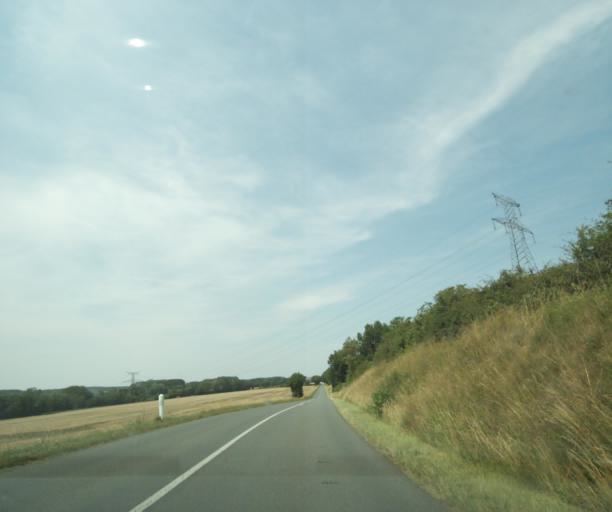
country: FR
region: Poitou-Charentes
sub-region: Departement de la Vienne
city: Lussac-les-Chateaux
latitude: 46.4626
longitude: 0.6644
